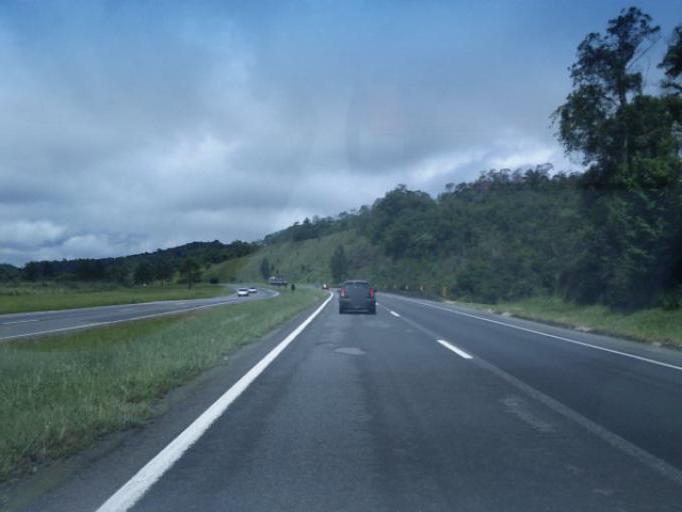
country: BR
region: Parana
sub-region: Antonina
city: Antonina
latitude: -25.0975
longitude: -48.6561
